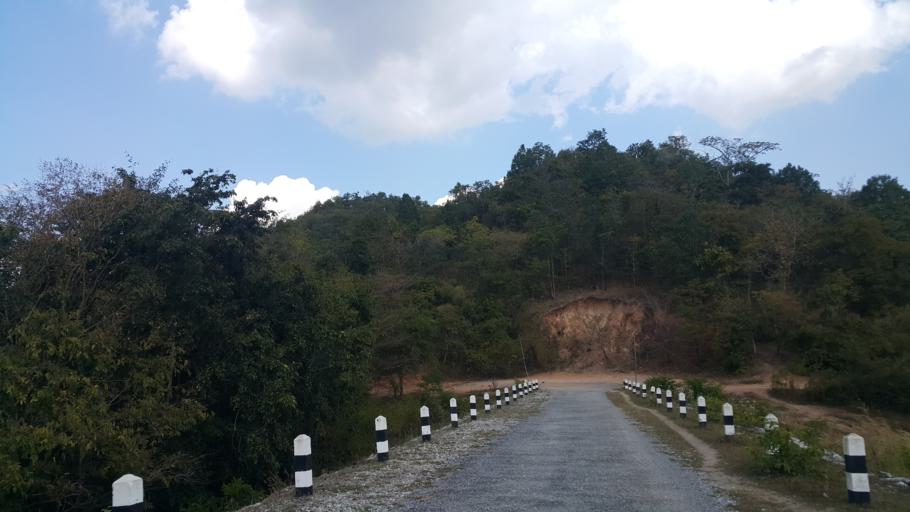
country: TH
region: Lamphun
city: Ban Thi
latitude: 18.5851
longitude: 99.1605
